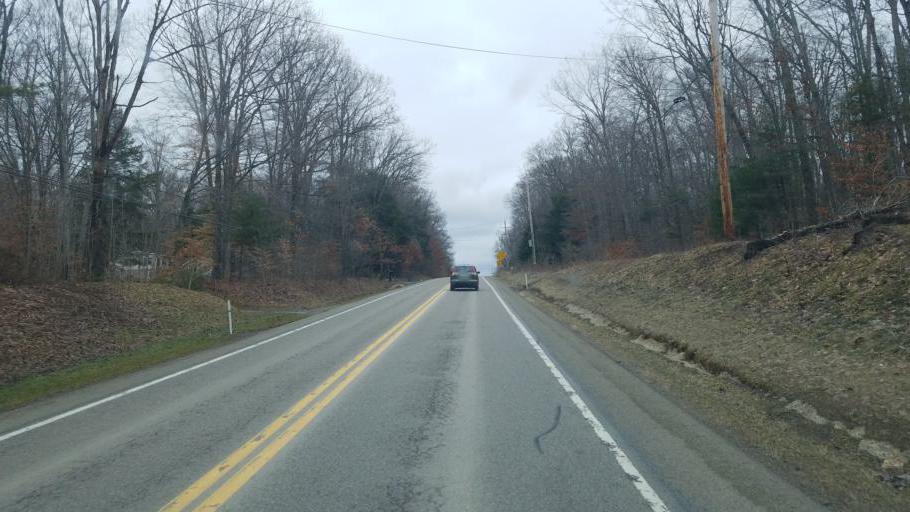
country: US
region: Pennsylvania
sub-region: Forest County
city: Marienville
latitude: 41.3816
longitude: -79.2833
